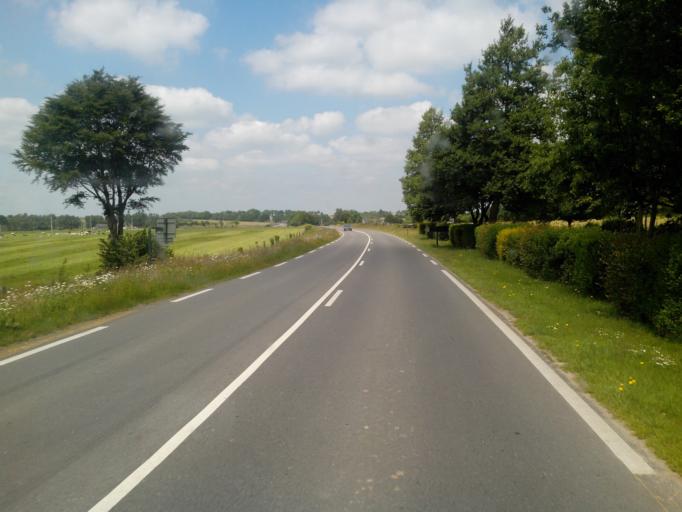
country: FR
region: Brittany
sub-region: Departement d'Ille-et-Vilaine
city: Saint-Germain-en-Cogles
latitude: 48.3922
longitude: -1.2848
